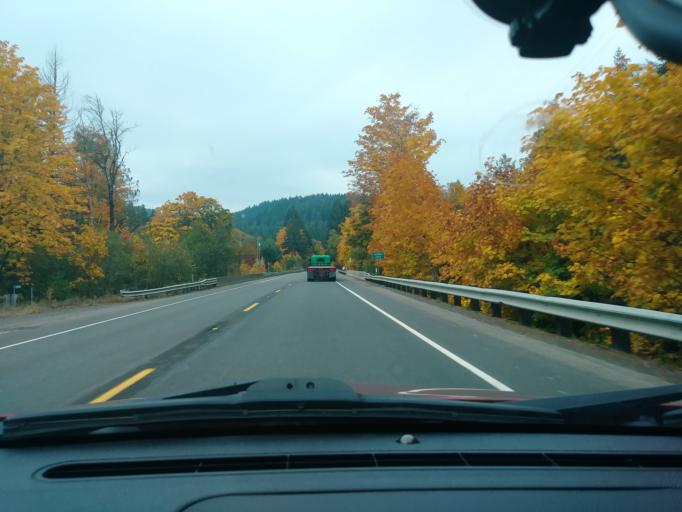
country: US
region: Oregon
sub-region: Washington County
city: Banks
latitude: 45.6248
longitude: -123.2635
